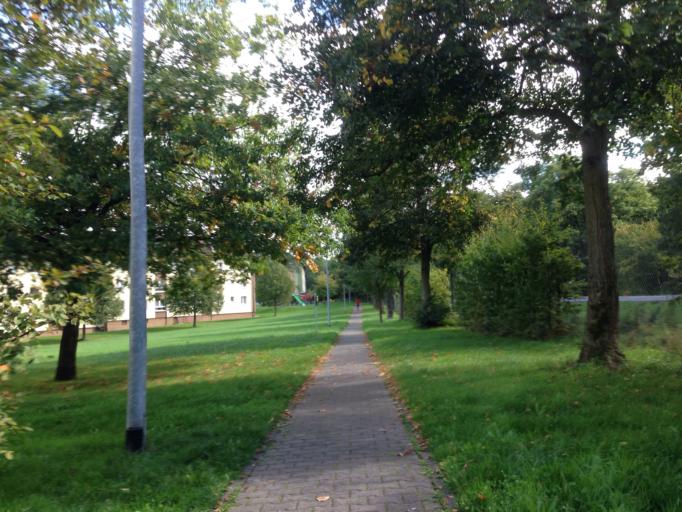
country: DE
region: Hesse
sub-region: Regierungsbezirk Giessen
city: Giessen
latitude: 50.5870
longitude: 8.7175
